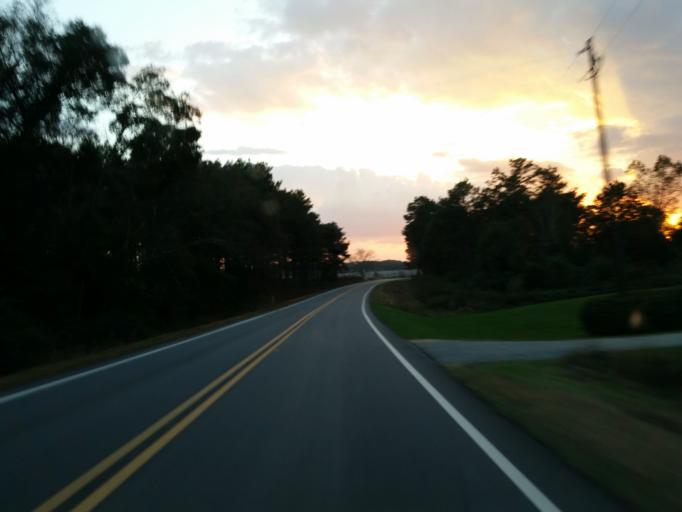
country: US
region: Georgia
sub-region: Pulaski County
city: Hawkinsville
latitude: 32.1766
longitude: -83.5939
